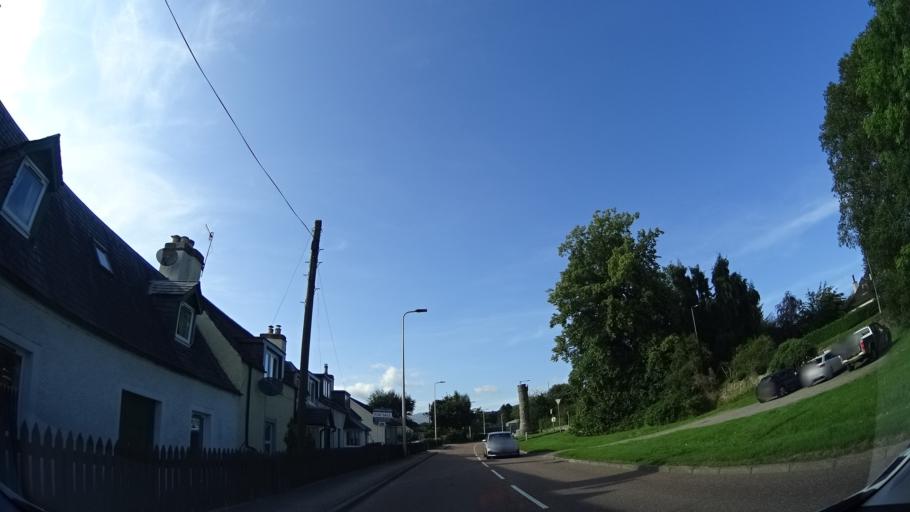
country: GB
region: Scotland
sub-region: Highland
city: Muir of Ord
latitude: 57.5657
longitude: -4.5786
